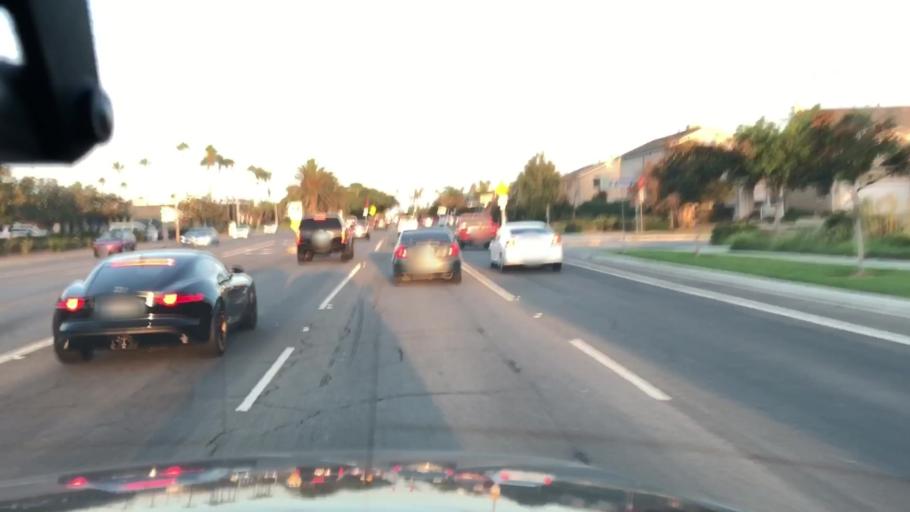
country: US
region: California
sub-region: Ventura County
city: El Rio
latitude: 34.2189
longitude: -119.1625
